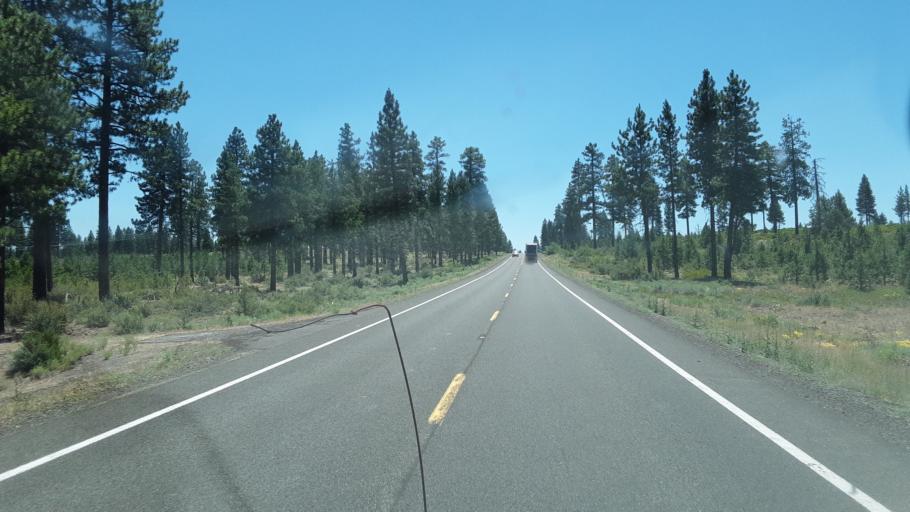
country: US
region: California
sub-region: Siskiyou County
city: Tulelake
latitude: 41.5980
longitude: -121.2026
